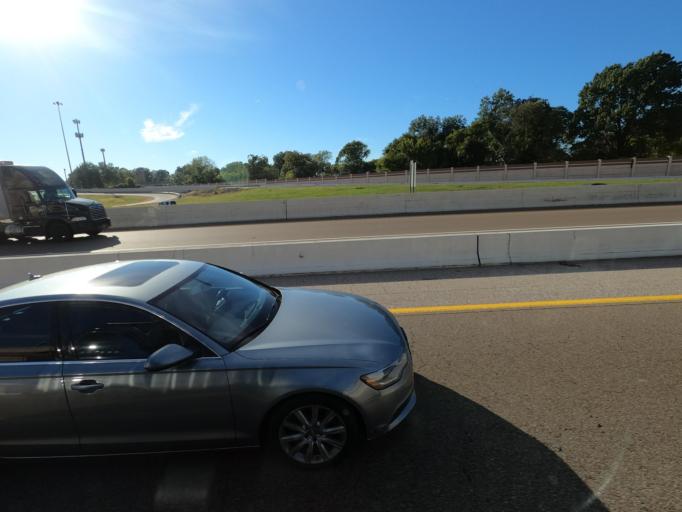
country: US
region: Tennessee
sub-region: Shelby County
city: Memphis
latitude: 35.1595
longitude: -90.0201
